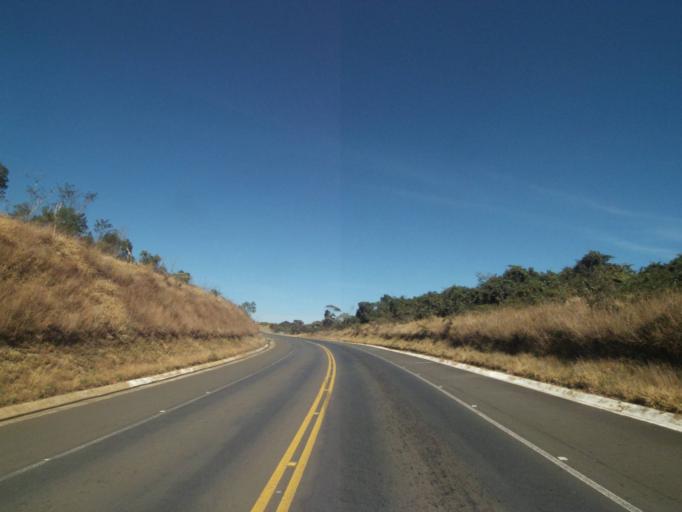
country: BR
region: Parana
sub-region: Tibagi
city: Tibagi
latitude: -24.7563
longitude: -50.4696
